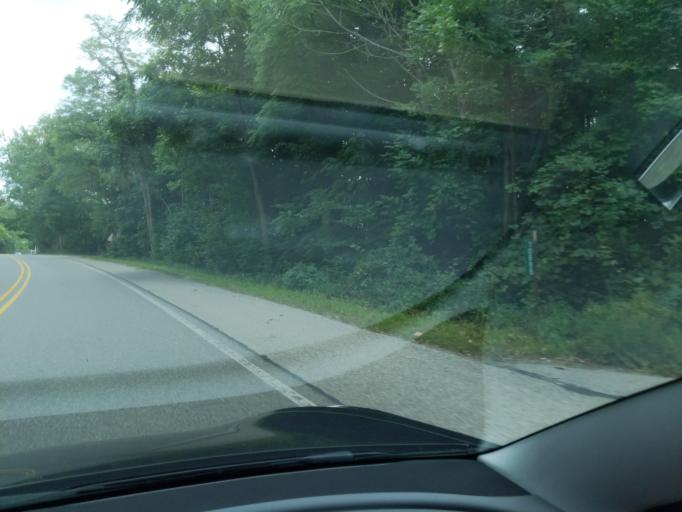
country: US
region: Michigan
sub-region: Kalkaska County
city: Rapid City
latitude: 44.8732
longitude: -85.2788
